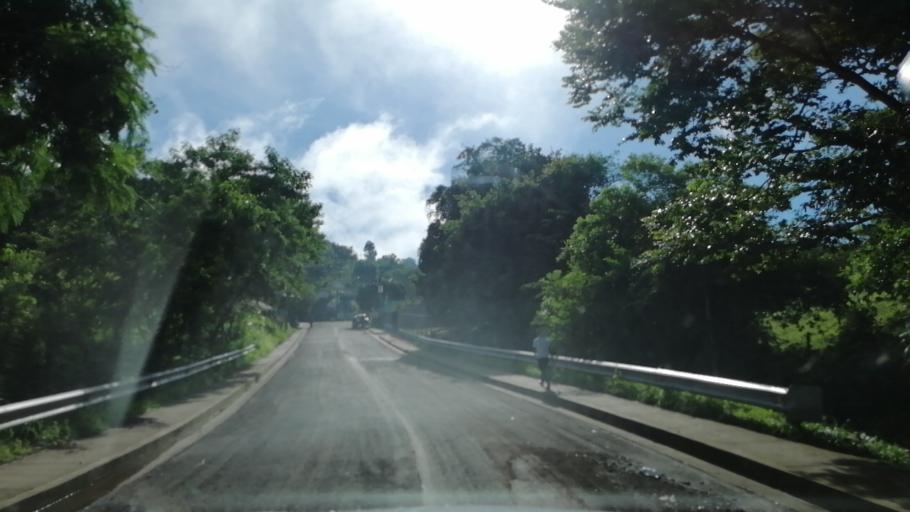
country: SV
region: Morazan
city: Cacaopera
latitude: 13.7748
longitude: -88.0857
